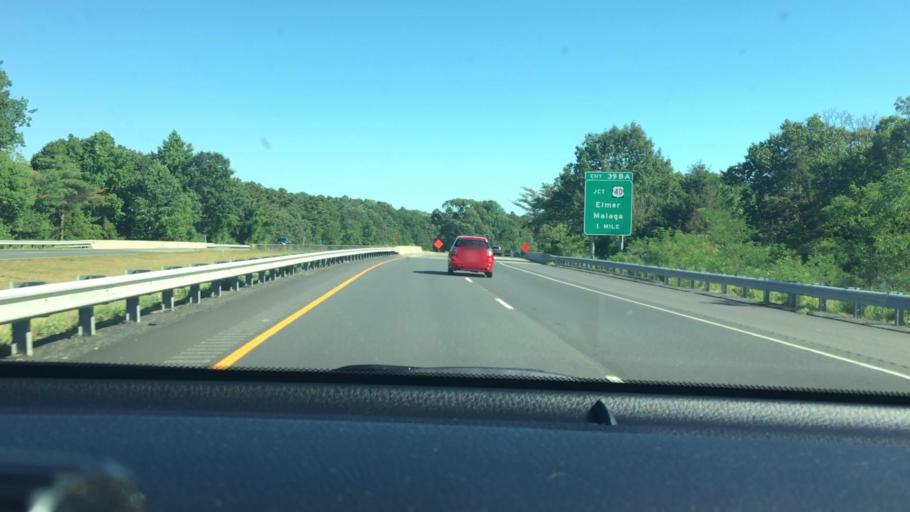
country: US
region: New Jersey
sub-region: Gloucester County
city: Clayton
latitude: 39.5981
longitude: -75.0746
